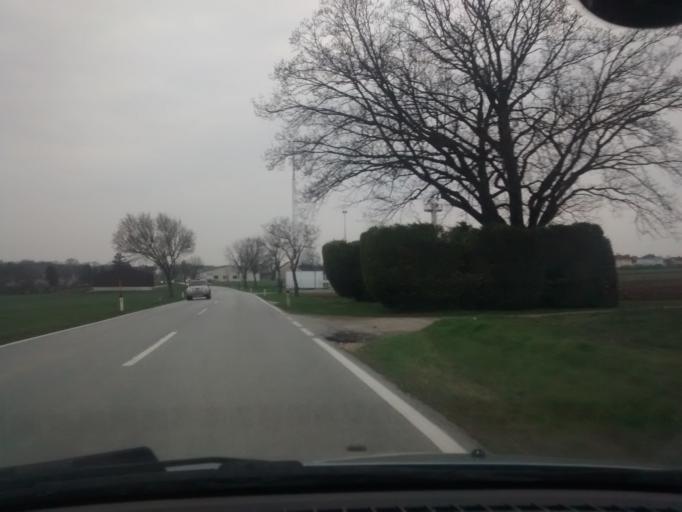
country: AT
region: Lower Austria
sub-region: Politischer Bezirk Wien-Umgebung
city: Gramatneusiedl
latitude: 48.0248
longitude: 16.4714
